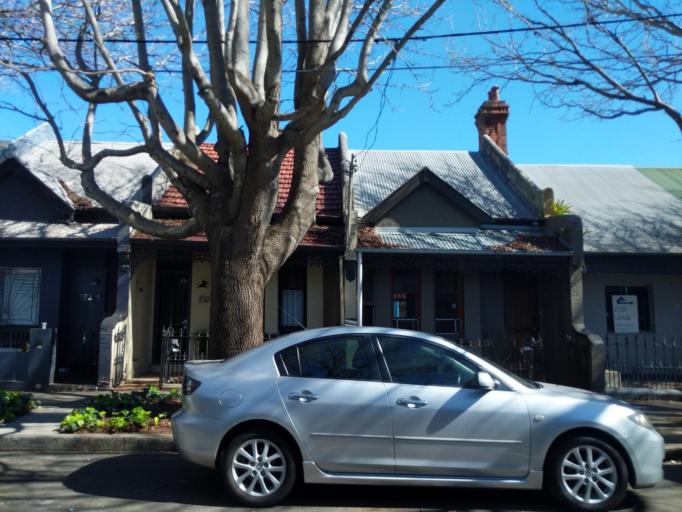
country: AU
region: New South Wales
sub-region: City of Sydney
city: Redfern
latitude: -33.8963
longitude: 151.2117
